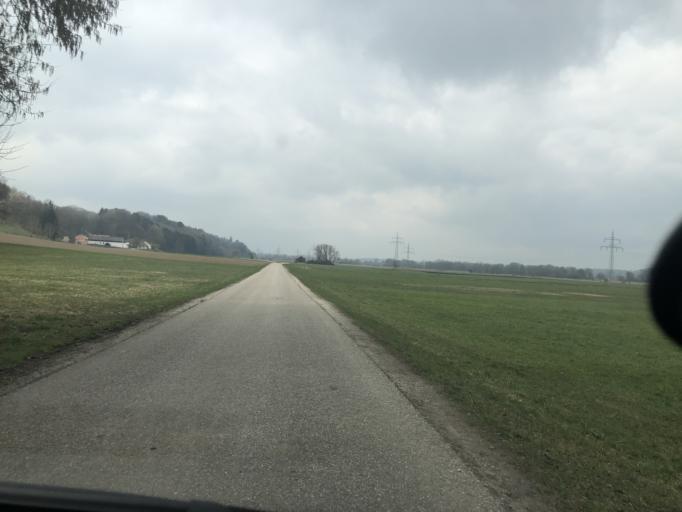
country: DE
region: Bavaria
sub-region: Upper Bavaria
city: Wolfersdorf
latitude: 48.4436
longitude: 11.6967
